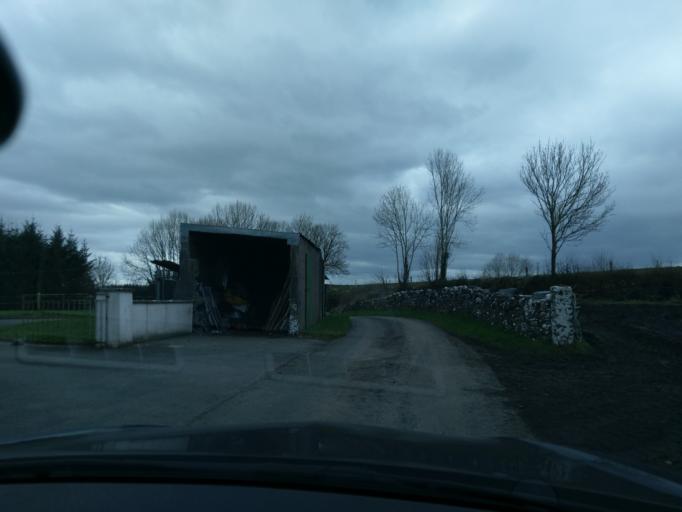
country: IE
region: Connaught
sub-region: County Galway
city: Athenry
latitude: 53.3769
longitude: -8.6350
